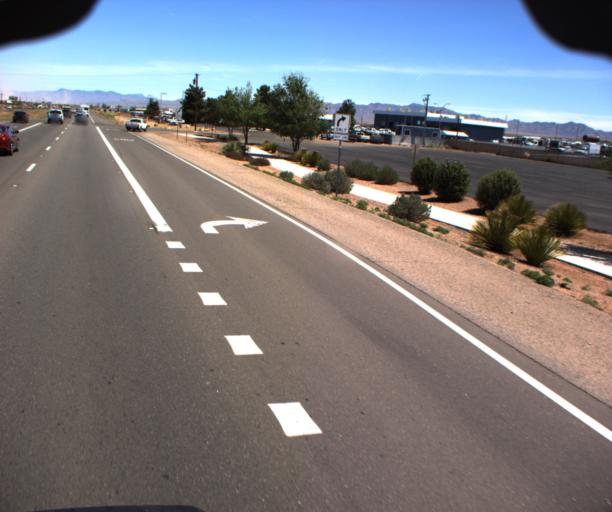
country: US
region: Arizona
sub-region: Mohave County
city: New Kingman-Butler
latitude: 35.2284
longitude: -113.9996
